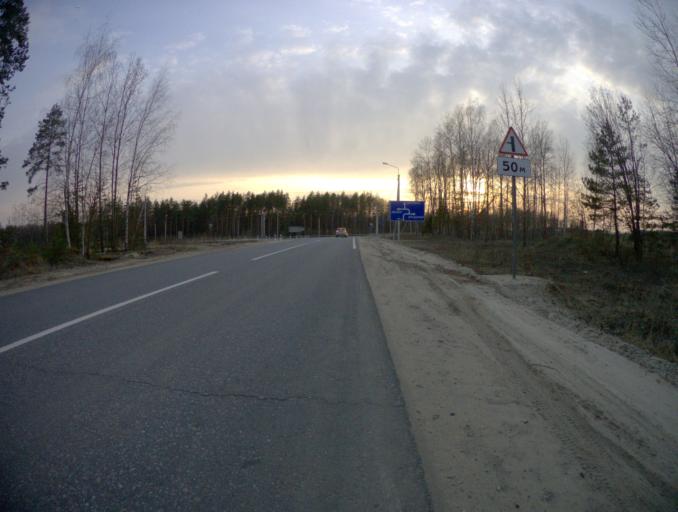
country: RU
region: Vladimir
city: Kommunar
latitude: 56.0682
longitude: 40.5018
